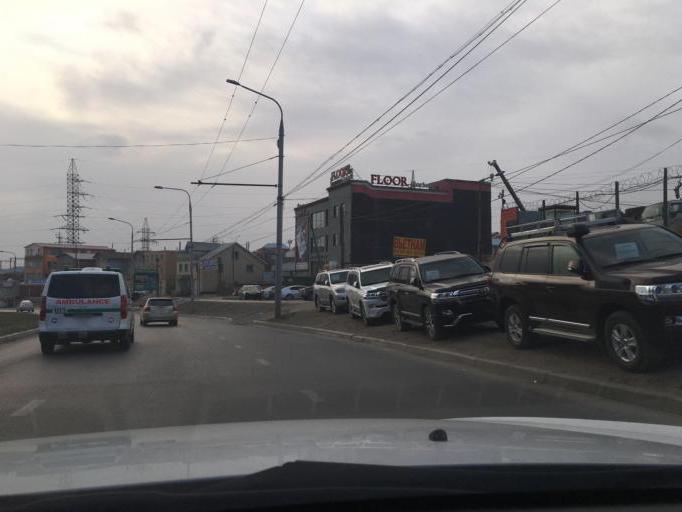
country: MN
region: Ulaanbaatar
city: Ulaanbaatar
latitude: 47.9213
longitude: 106.8568
